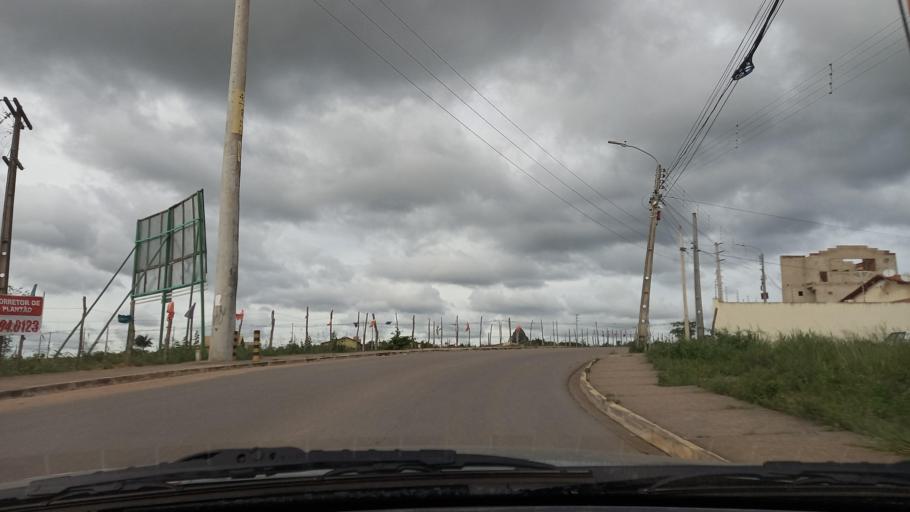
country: BR
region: Pernambuco
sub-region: Gravata
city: Gravata
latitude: -8.2023
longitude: -35.5503
